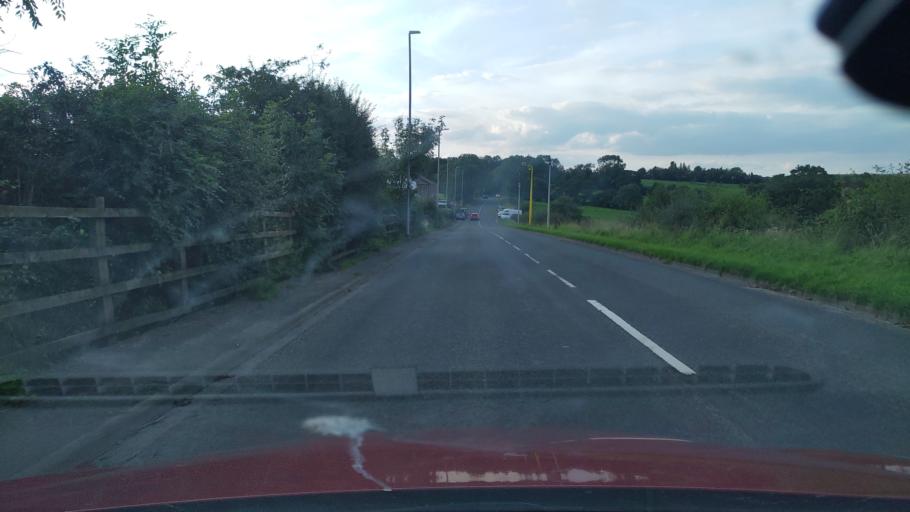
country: GB
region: England
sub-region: Blackburn with Darwen
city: Blackburn
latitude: 53.7010
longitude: -2.5477
